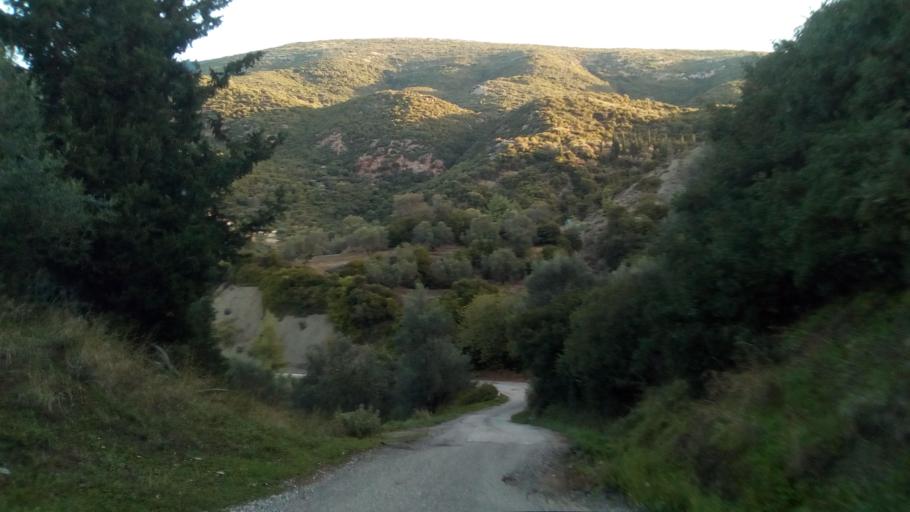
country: GR
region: West Greece
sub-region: Nomos Aitolias kai Akarnanias
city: Nafpaktos
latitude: 38.4056
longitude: 21.7995
